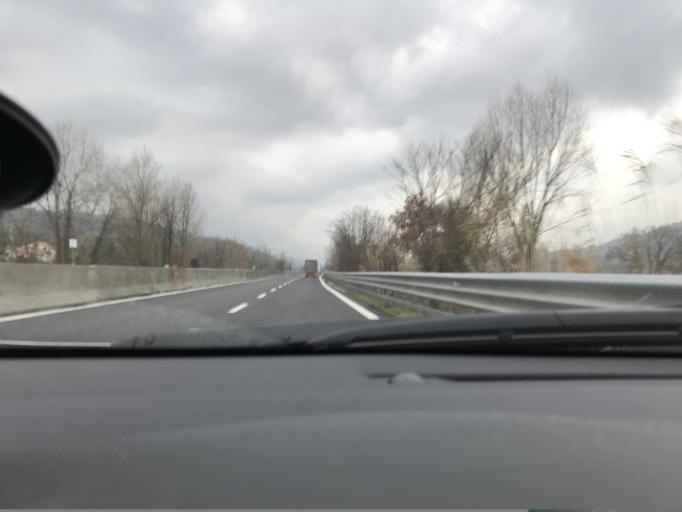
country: IT
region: The Marches
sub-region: Provincia di Ancona
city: Macine-Borgo Loreto
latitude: 43.4876
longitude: 13.0993
